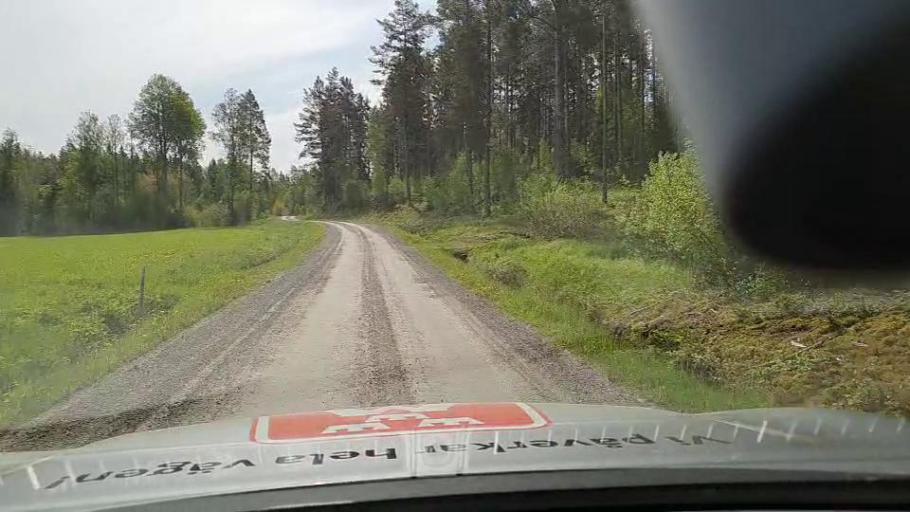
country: SE
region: Soedermanland
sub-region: Eskilstuna Kommun
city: Arla
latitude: 59.2620
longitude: 16.8233
